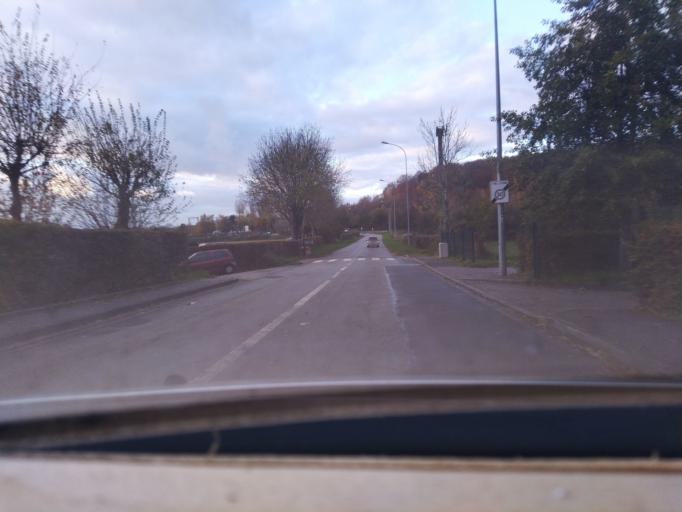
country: FR
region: Haute-Normandie
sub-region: Departement de la Seine-Maritime
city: Yainville
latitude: 49.4566
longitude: 0.8276
